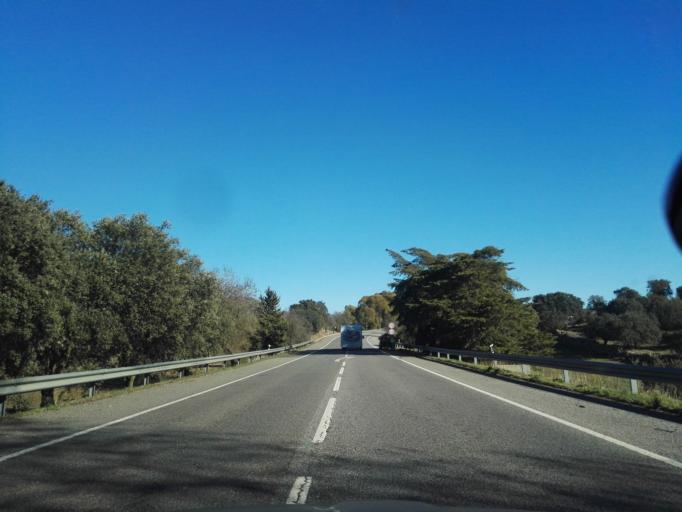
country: PT
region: Evora
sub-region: Vila Vicosa
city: Vila Vicosa
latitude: 38.8483
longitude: -7.3529
